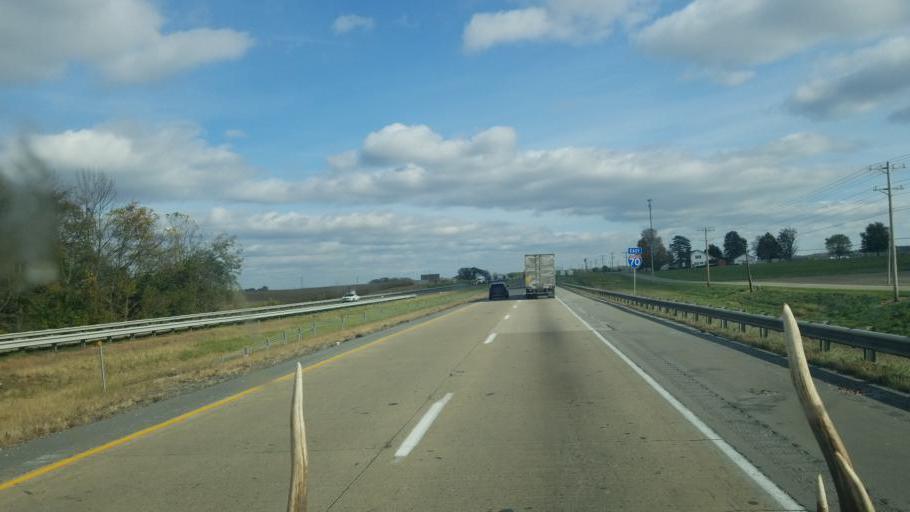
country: US
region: Indiana
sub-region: Wayne County
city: Cambridge City
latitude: 39.8527
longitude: -85.1344
